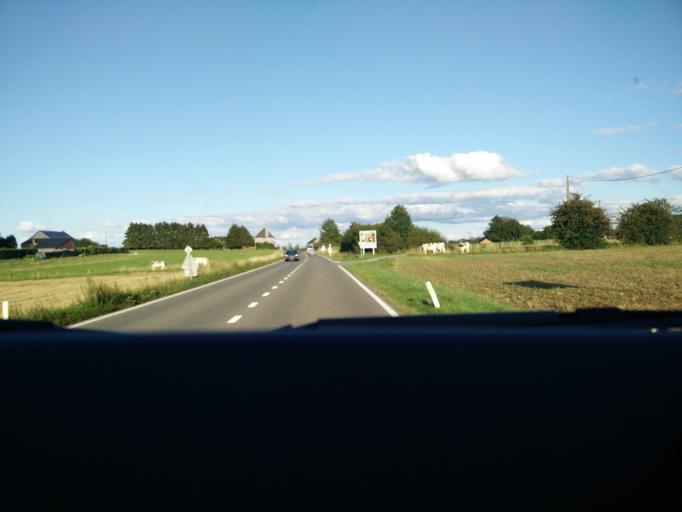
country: BE
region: Wallonia
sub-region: Province de Namur
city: Hastiere-Lavaux
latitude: 50.2361
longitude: 4.7342
